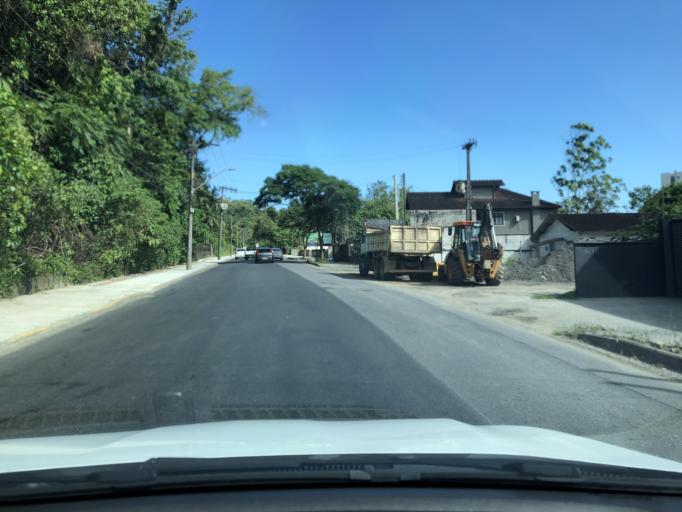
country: BR
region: Santa Catarina
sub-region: Joinville
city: Joinville
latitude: -26.3092
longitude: -48.8350
